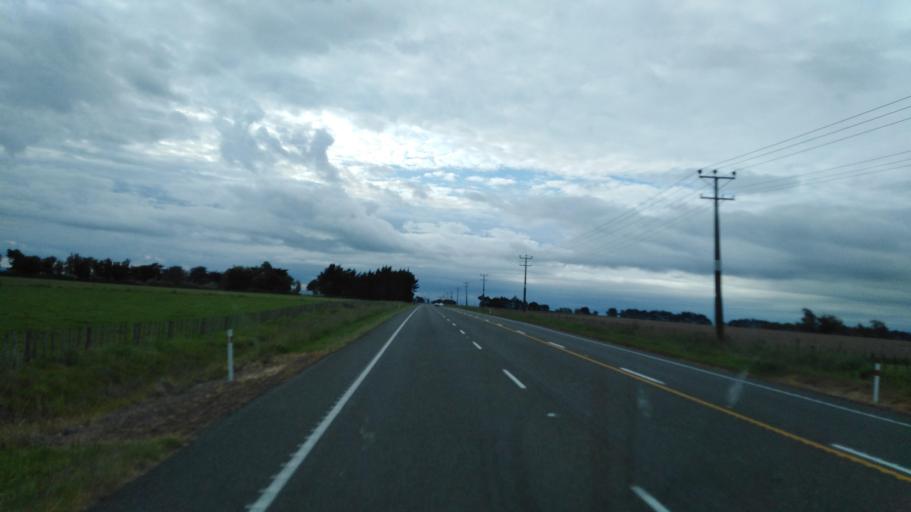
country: NZ
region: Manawatu-Wanganui
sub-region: Rangitikei District
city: Bulls
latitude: -40.1279
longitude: 175.3567
